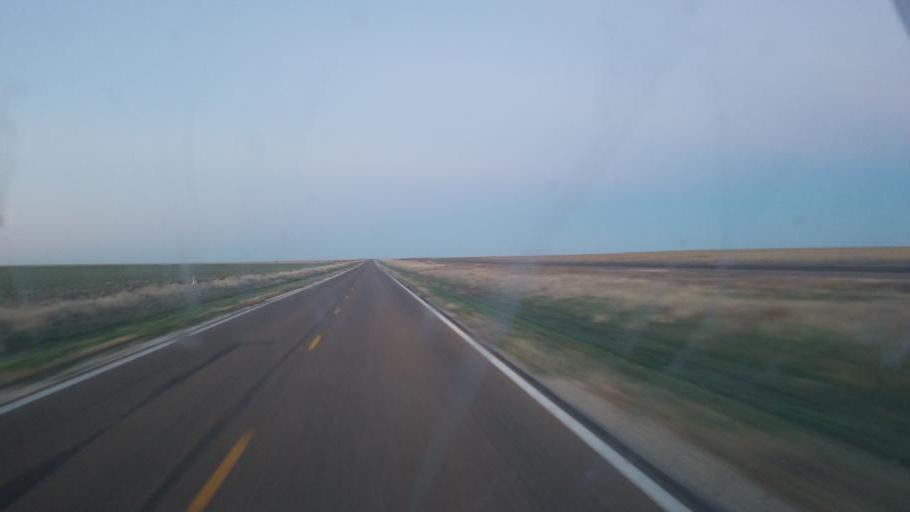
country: US
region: Kansas
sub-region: Wallace County
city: Sharon Springs
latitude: 38.9917
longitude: -101.4111
